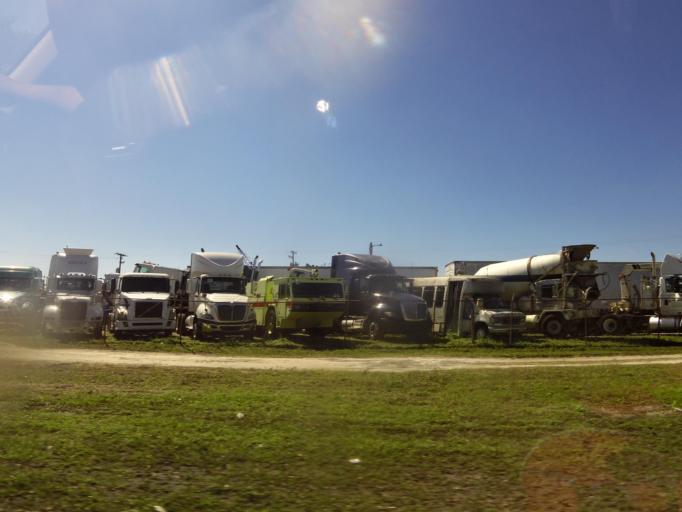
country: US
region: Florida
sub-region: Orange County
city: Lockhart
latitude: 28.6304
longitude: -81.4504
